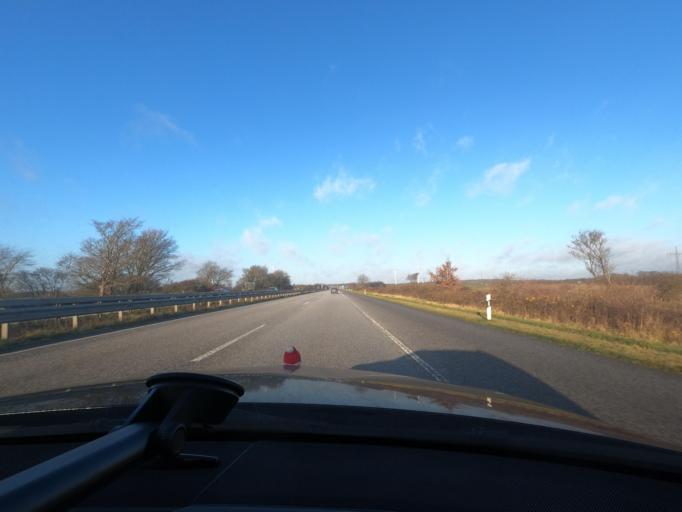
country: DE
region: Schleswig-Holstein
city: Bollingstedt
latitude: 54.6282
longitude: 9.4408
